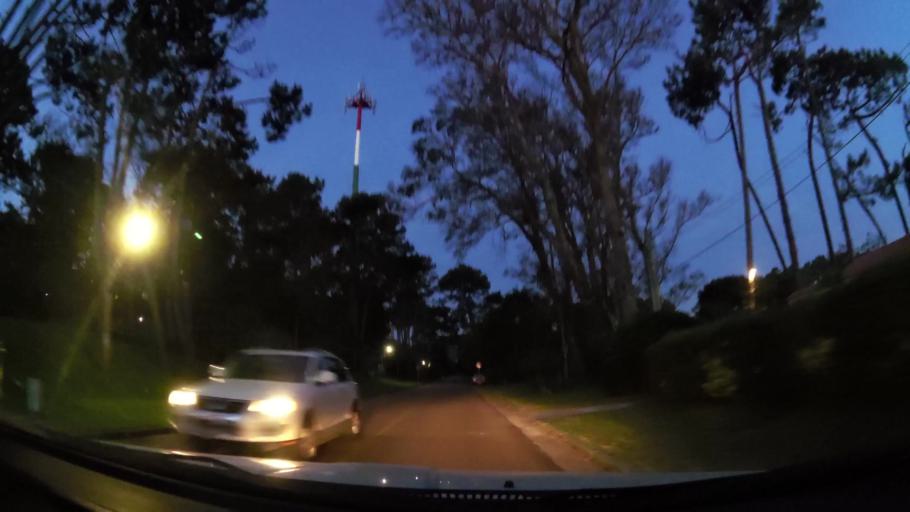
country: UY
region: Maldonado
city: Punta del Este
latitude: -34.9383
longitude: -54.9188
